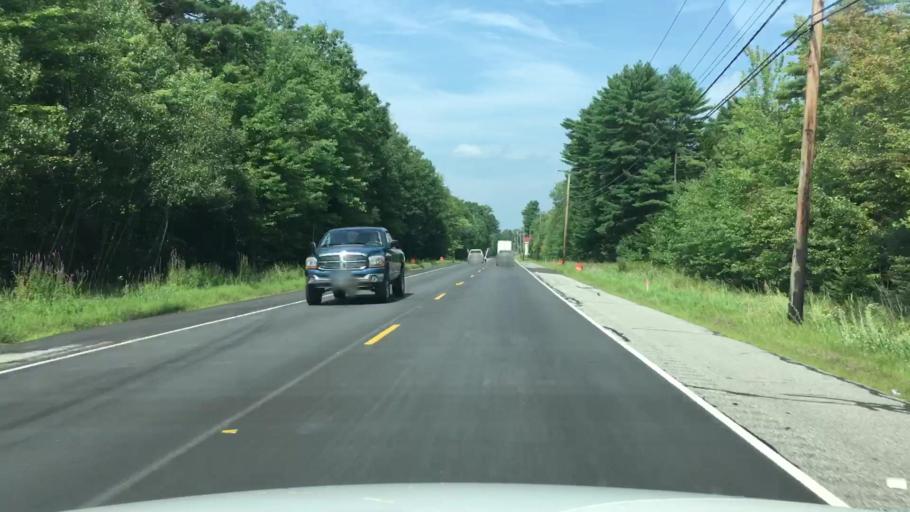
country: US
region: Maine
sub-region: Androscoggin County
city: Turner
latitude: 44.2352
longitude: -70.2565
